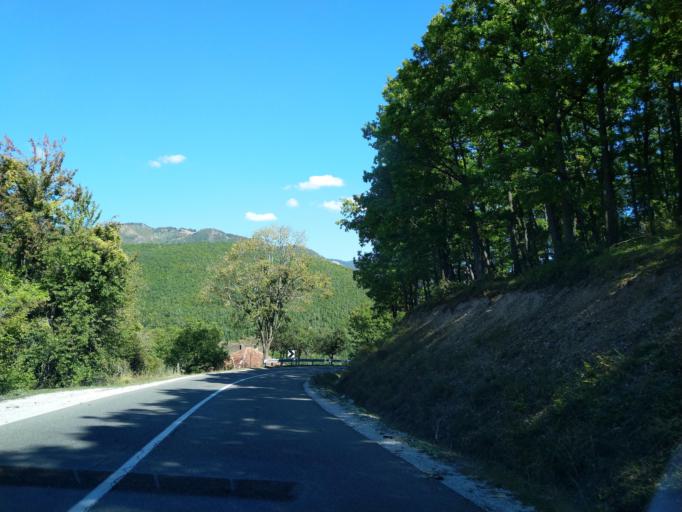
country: RS
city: Sokolovica
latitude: 43.2552
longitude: 20.2528
